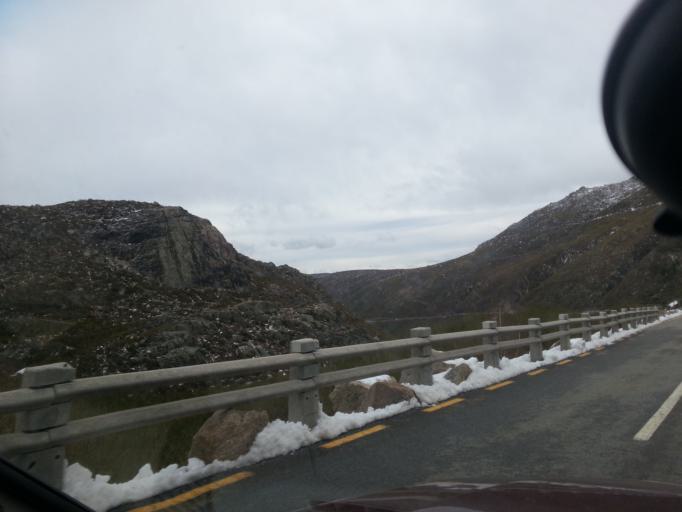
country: PT
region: Guarda
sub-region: Manteigas
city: Manteigas
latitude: 40.3261
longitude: -7.5821
